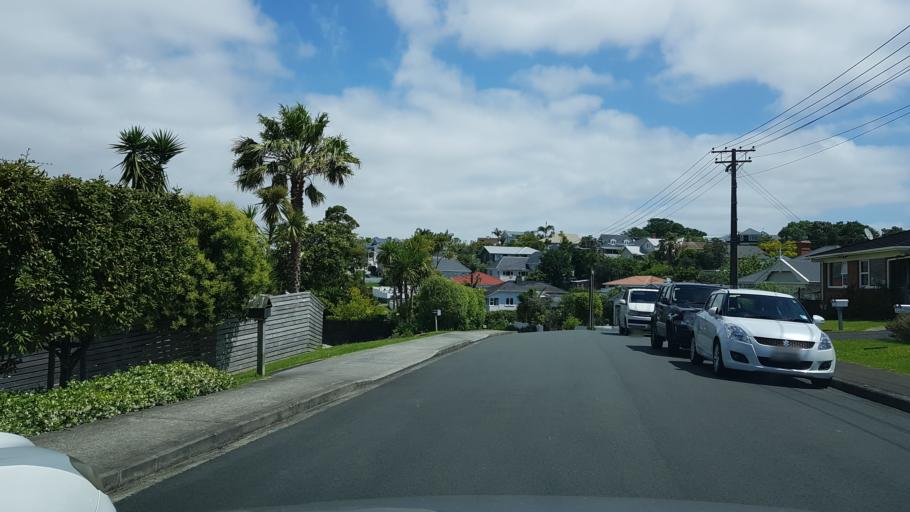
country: NZ
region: Auckland
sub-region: Auckland
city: North Shore
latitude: -36.8135
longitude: 174.7466
